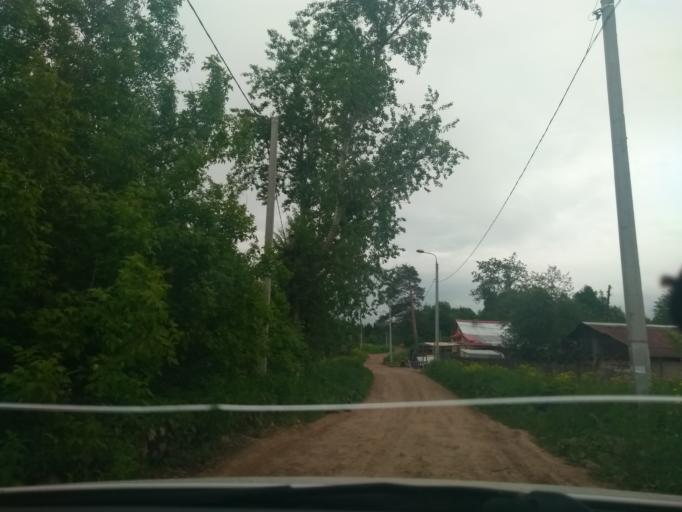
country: RU
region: Perm
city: Perm
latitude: 57.9905
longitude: 56.3381
